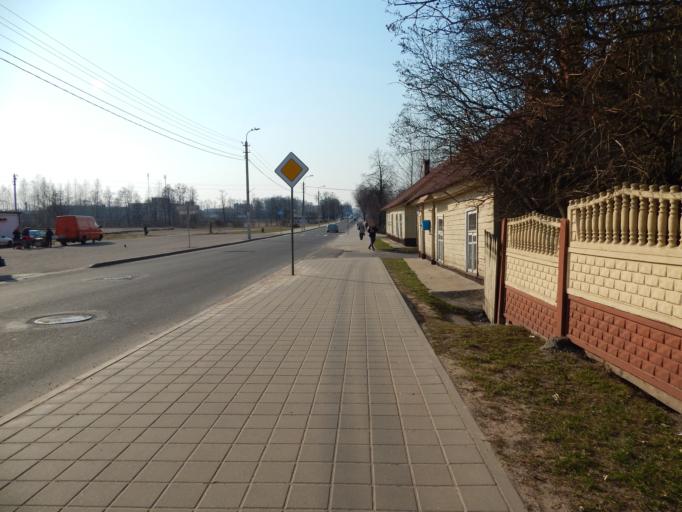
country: BY
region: Minsk
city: Zaslawye
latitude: 54.0052
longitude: 27.2891
